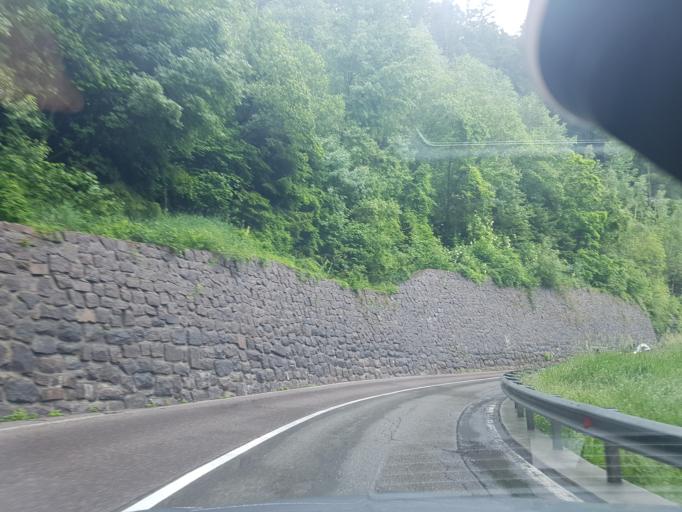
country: IT
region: Trentino-Alto Adige
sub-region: Bolzano
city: Laion
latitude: 46.6005
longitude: 11.6144
